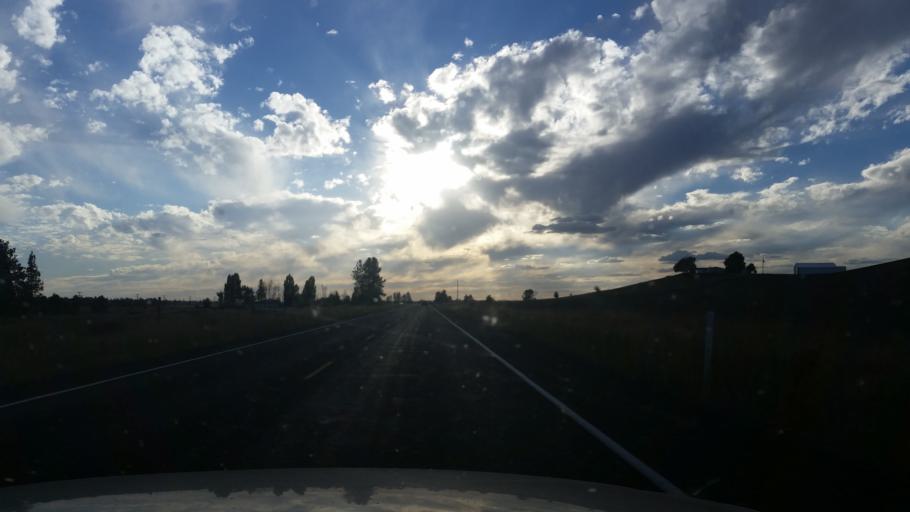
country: US
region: Washington
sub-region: Spokane County
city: Cheney
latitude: 47.4698
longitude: -117.6243
